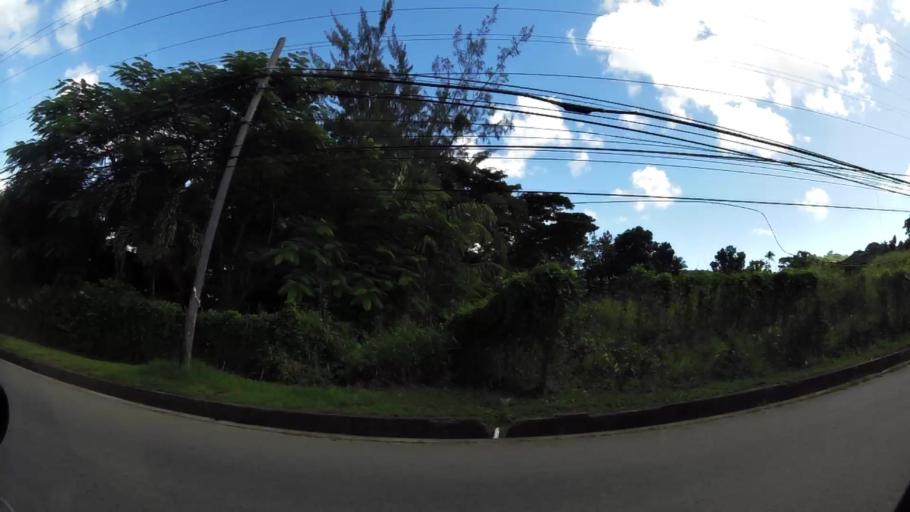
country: TT
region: Tobago
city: Scarborough
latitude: 11.2086
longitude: -60.7796
